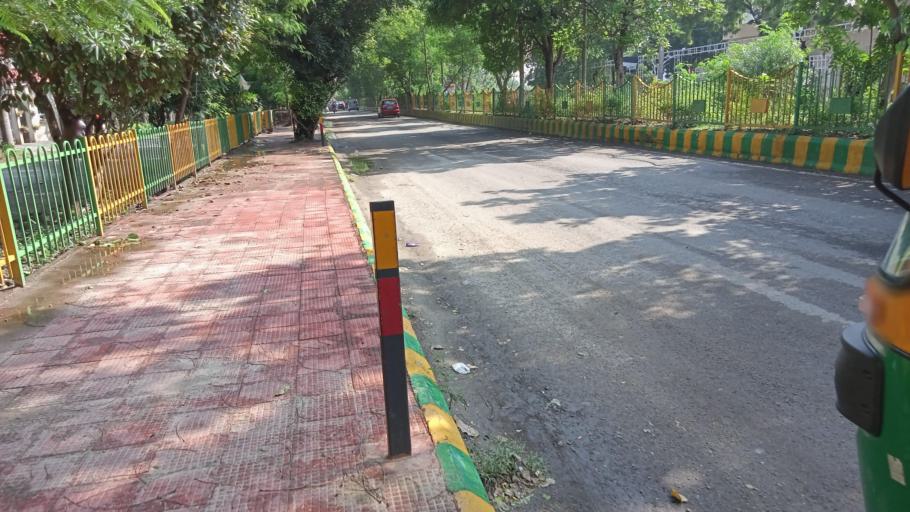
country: IN
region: Uttar Pradesh
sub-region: Ghaziabad
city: Ghaziabad
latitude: 28.6647
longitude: 77.3722
